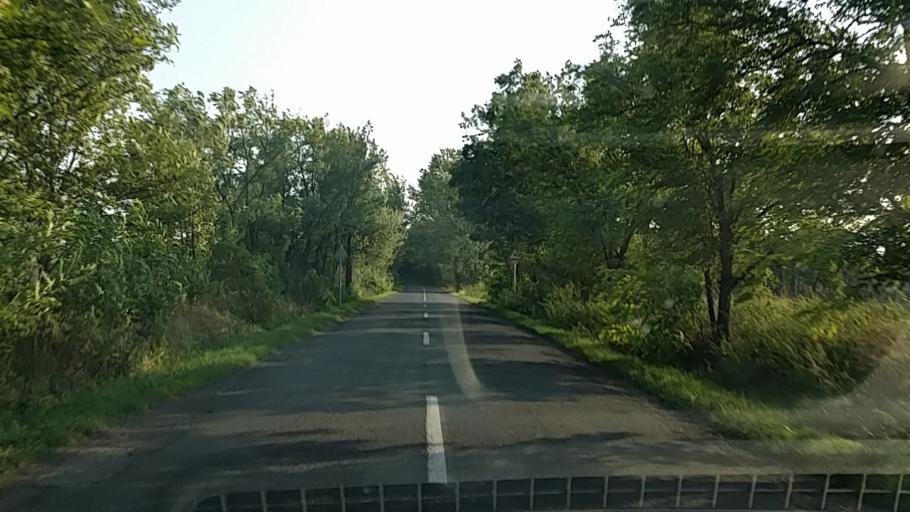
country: HU
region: Nograd
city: Hehalom
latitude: 47.7531
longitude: 19.5780
